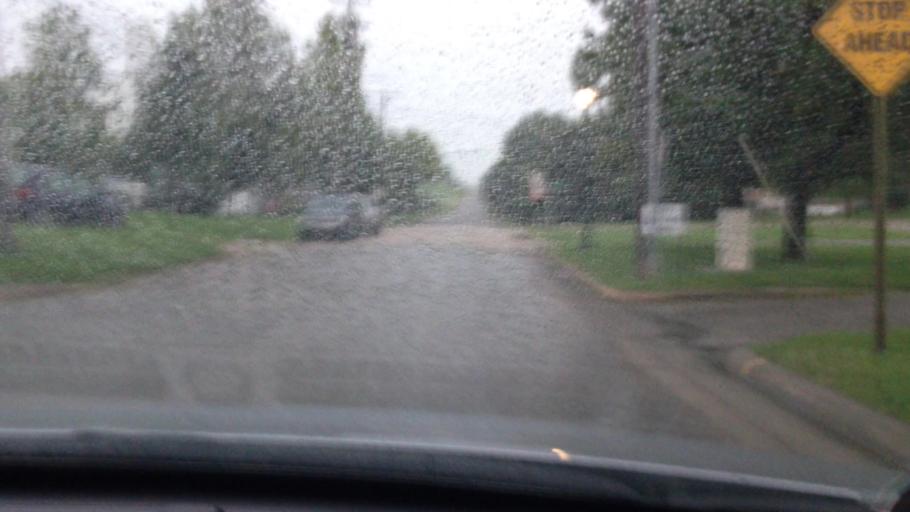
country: US
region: Kansas
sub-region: Brown County
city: Hiawatha
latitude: 39.8493
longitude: -95.5459
